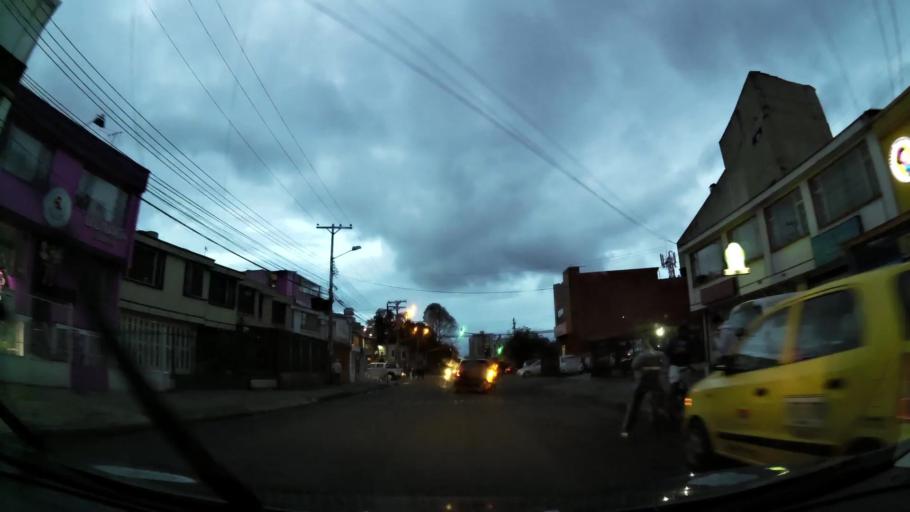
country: CO
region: Bogota D.C.
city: Bogota
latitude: 4.6733
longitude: -74.1088
